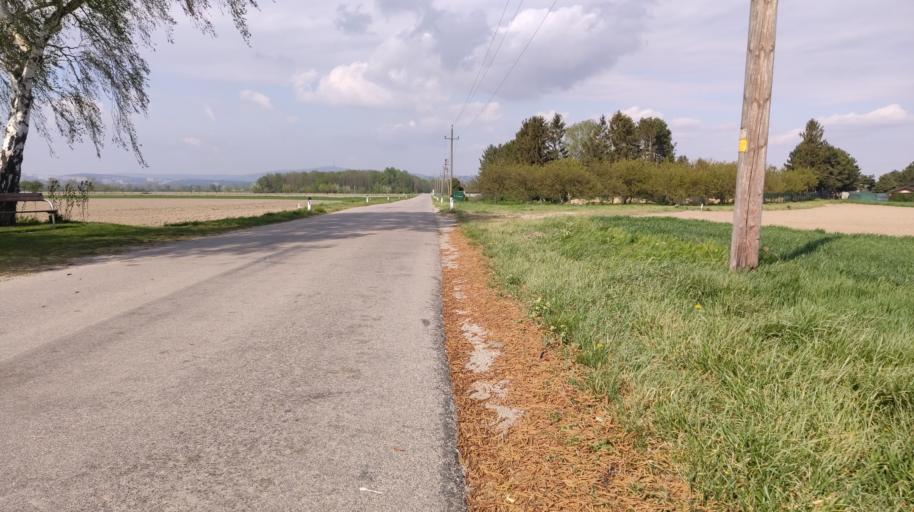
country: AT
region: Lower Austria
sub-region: Politischer Bezirk Bruck an der Leitha
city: Berg
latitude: 48.1101
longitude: 17.0518
